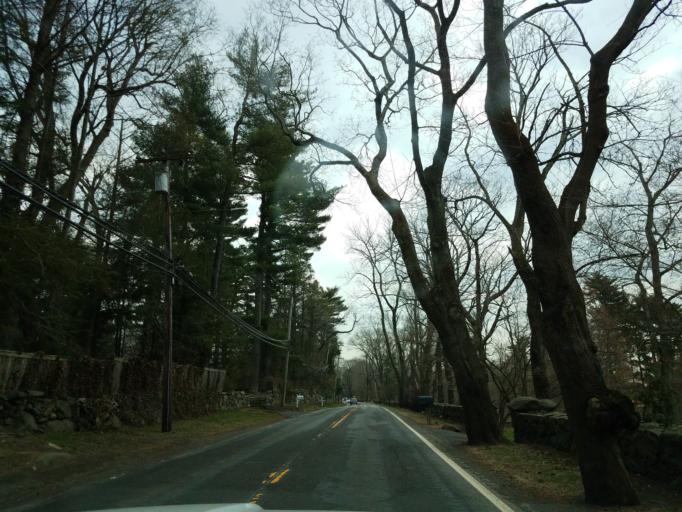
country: US
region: Connecticut
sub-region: Fairfield County
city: Glenville
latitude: 41.0532
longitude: -73.6390
